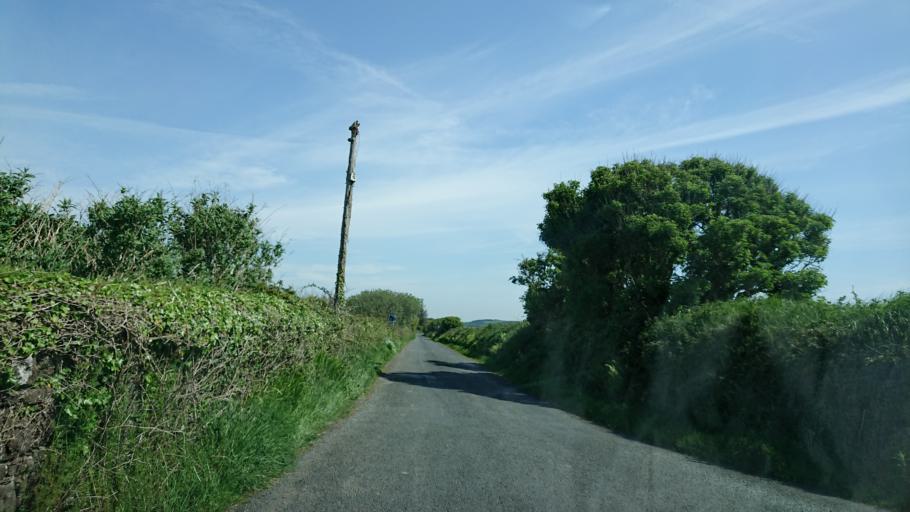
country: IE
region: Munster
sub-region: Waterford
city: Tra Mhor
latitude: 52.1507
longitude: -7.0766
